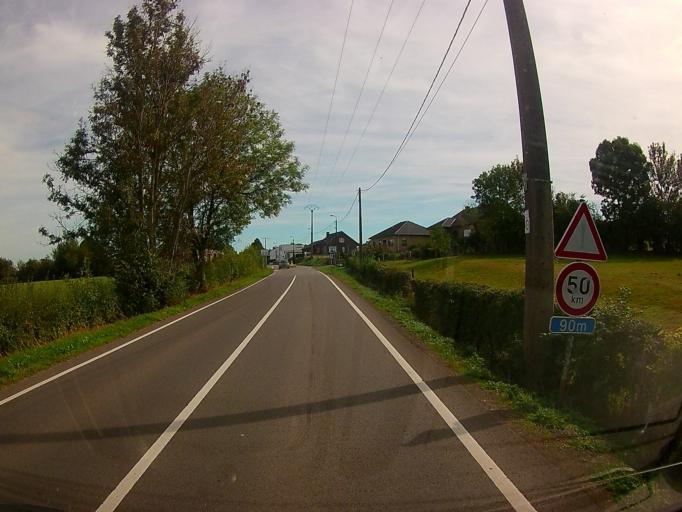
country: BE
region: Wallonia
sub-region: Province de Liege
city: Welkenraedt
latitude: 50.6789
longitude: 5.9214
